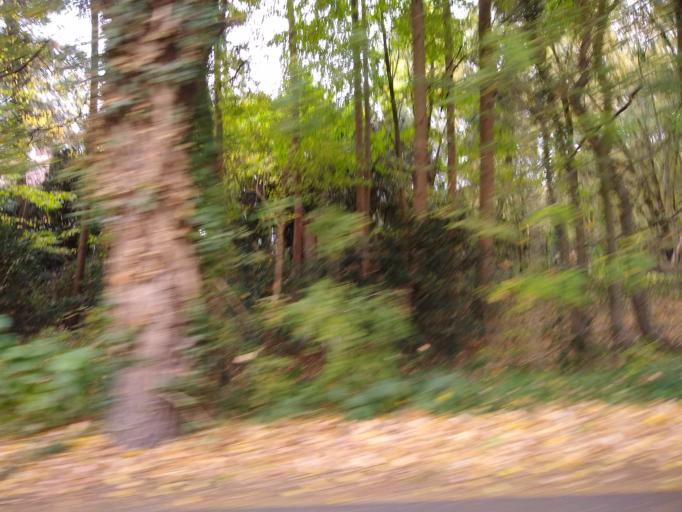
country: DE
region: Lower Saxony
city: Oldenburg
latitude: 53.1891
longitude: 8.2412
